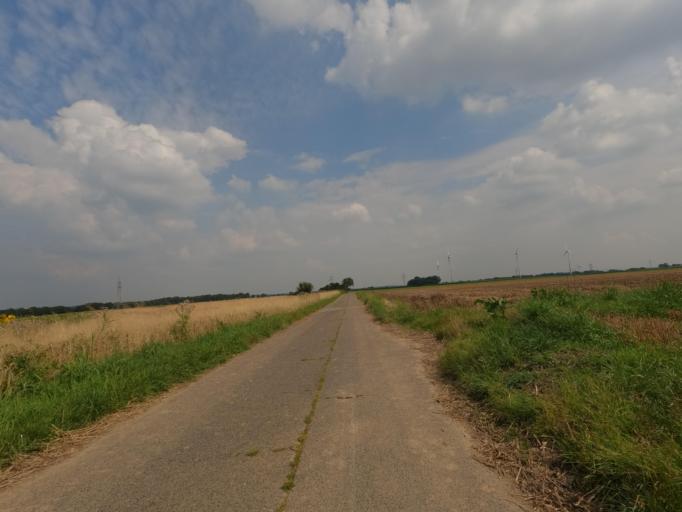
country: DE
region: North Rhine-Westphalia
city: Huckelhoven
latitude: 51.0108
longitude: 6.2063
